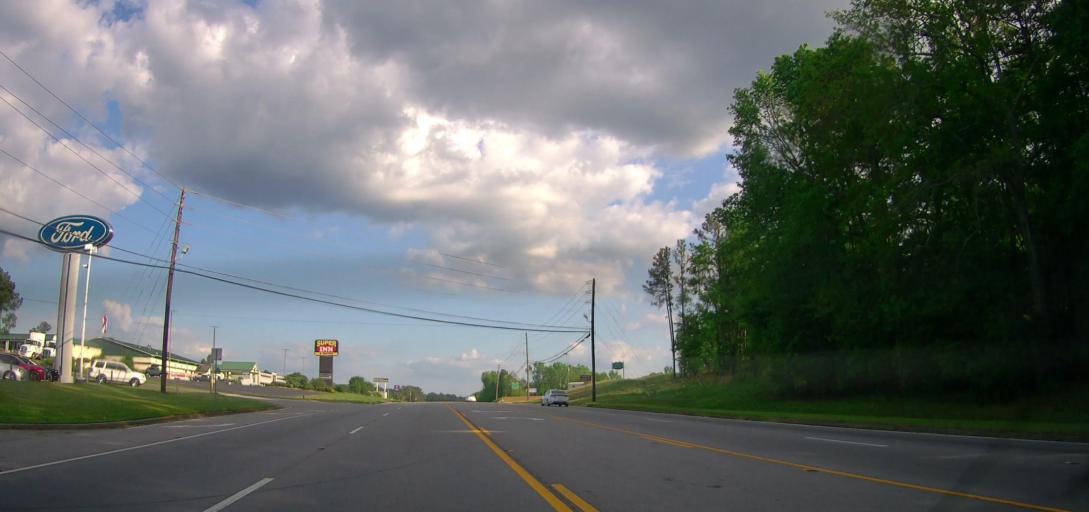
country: US
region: Georgia
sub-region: Baldwin County
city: Milledgeville
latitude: 33.1265
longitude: -83.2656
